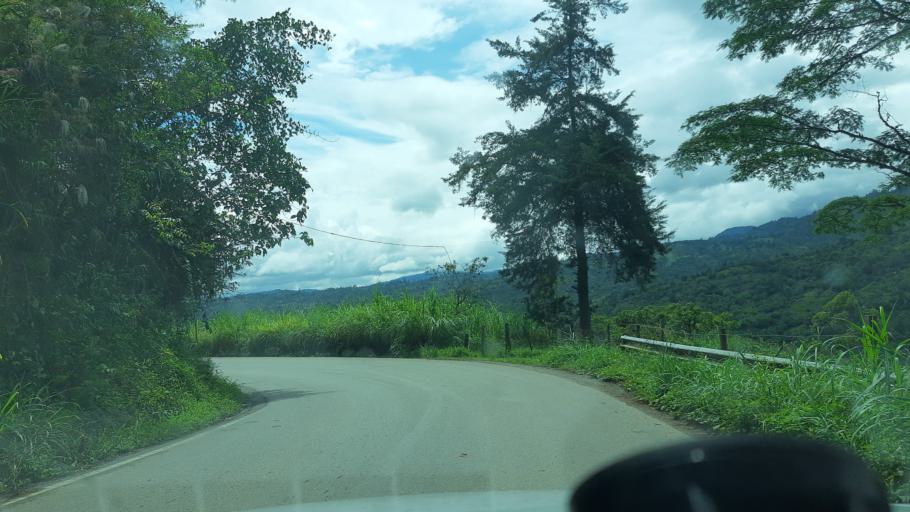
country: CO
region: Boyaca
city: Garagoa
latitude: 5.1037
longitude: -73.3680
